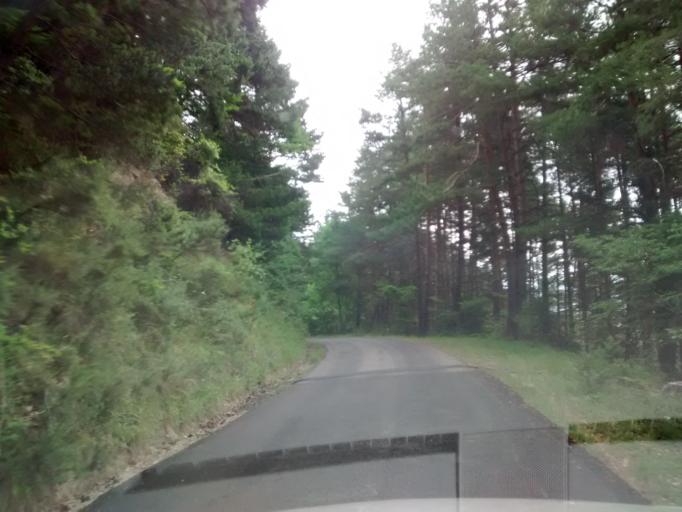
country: ES
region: Aragon
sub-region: Provincia de Huesca
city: Puertolas
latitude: 42.5755
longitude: 0.1398
